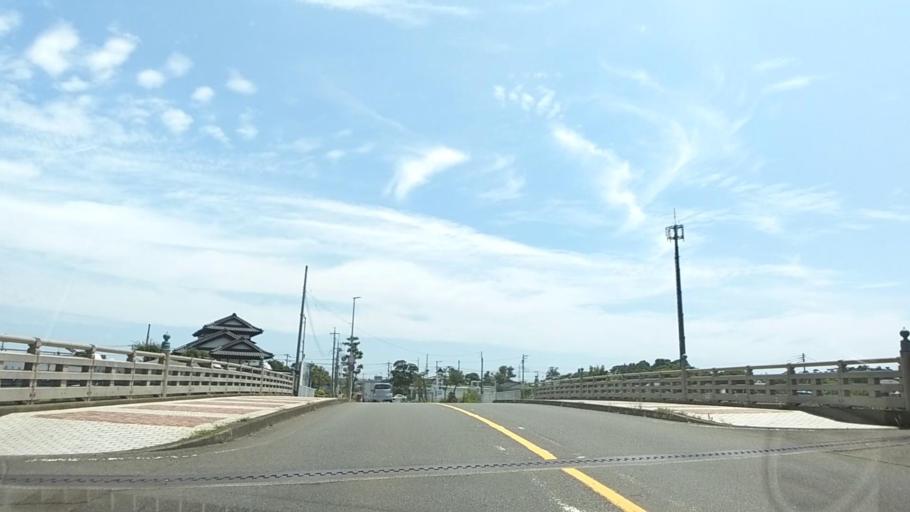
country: JP
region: Kanagawa
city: Atsugi
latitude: 35.3835
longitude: 139.3826
